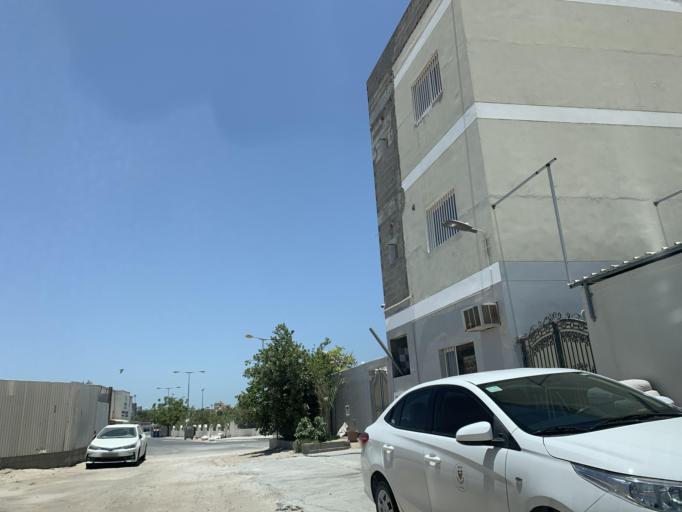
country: BH
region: Manama
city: Jidd Hafs
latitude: 26.2278
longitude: 50.4834
